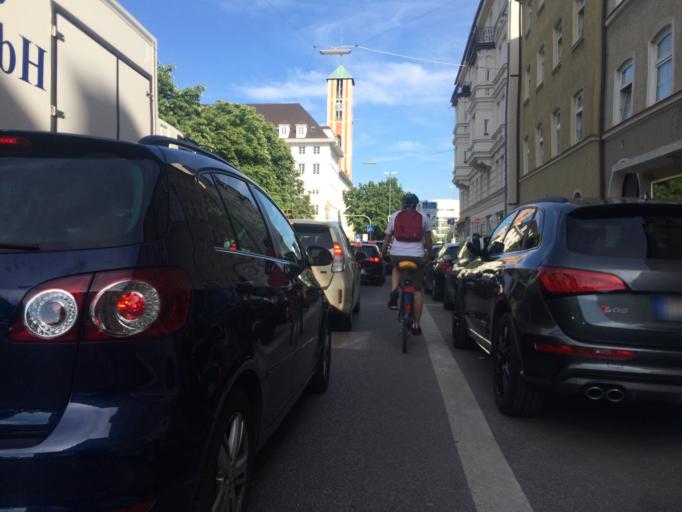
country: DE
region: Bavaria
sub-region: Upper Bavaria
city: Munich
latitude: 48.1464
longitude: 11.5721
